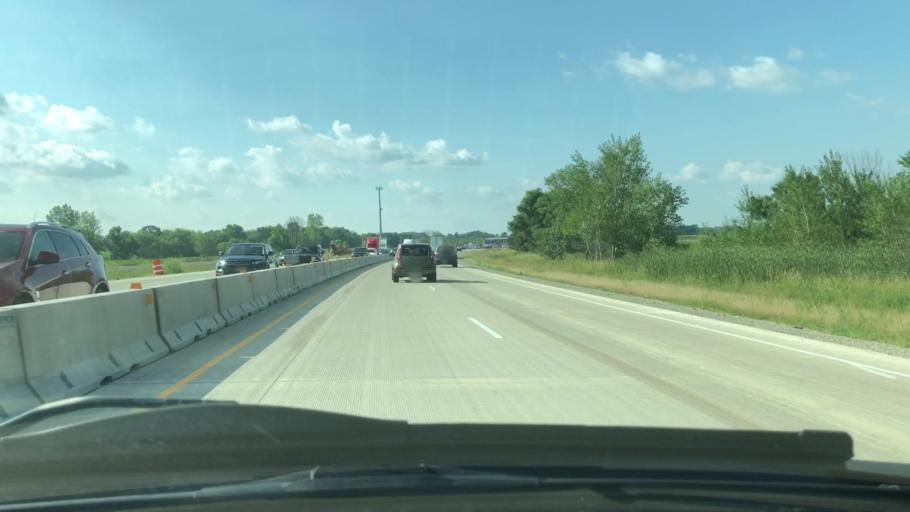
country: US
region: Wisconsin
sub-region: Rock County
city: Edgerton
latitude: 42.9066
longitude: -89.0838
